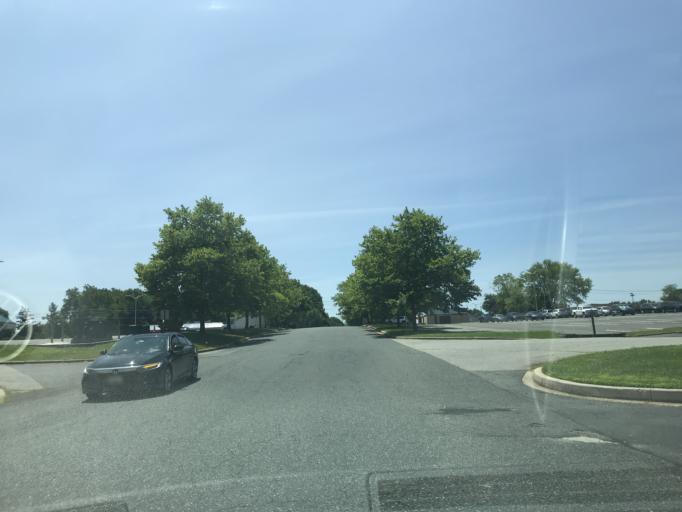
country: US
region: Maryland
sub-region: Harford County
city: South Bel Air
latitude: 39.5574
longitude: -76.2751
